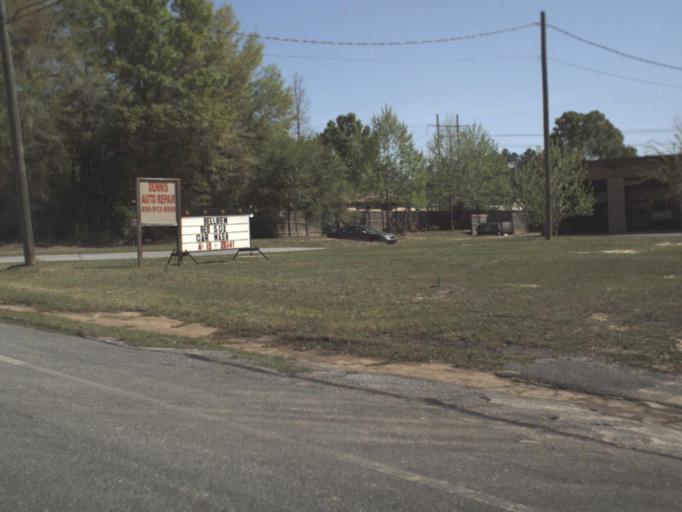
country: US
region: Florida
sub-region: Escambia County
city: Bellview
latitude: 30.4972
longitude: -87.3324
